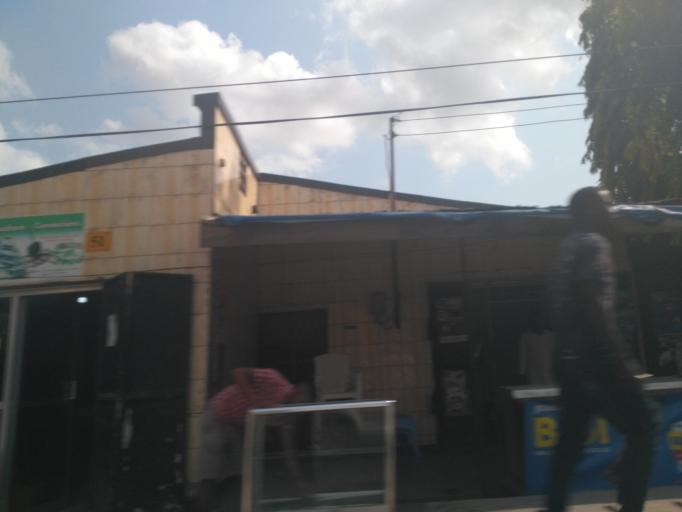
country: TZ
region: Dar es Salaam
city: Magomeni
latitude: -6.7799
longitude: 39.2476
